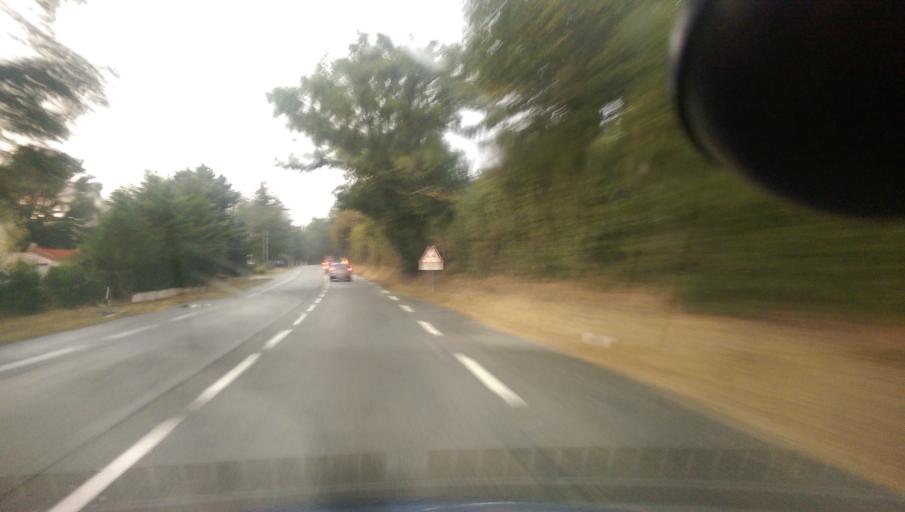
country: FR
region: Provence-Alpes-Cote d'Azur
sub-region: Departement des Alpes-Maritimes
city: Saint-Vallier-de-Thiey
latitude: 43.6869
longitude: 6.8771
